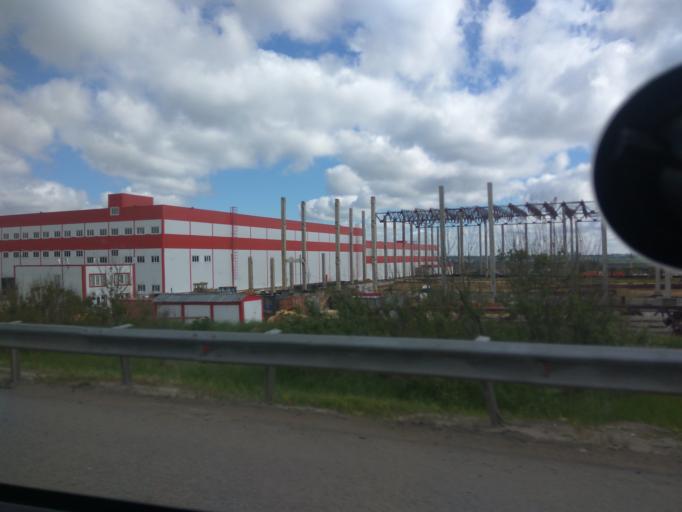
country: RU
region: Moskovskaya
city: Zhukovskiy
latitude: 55.5497
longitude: 38.0717
